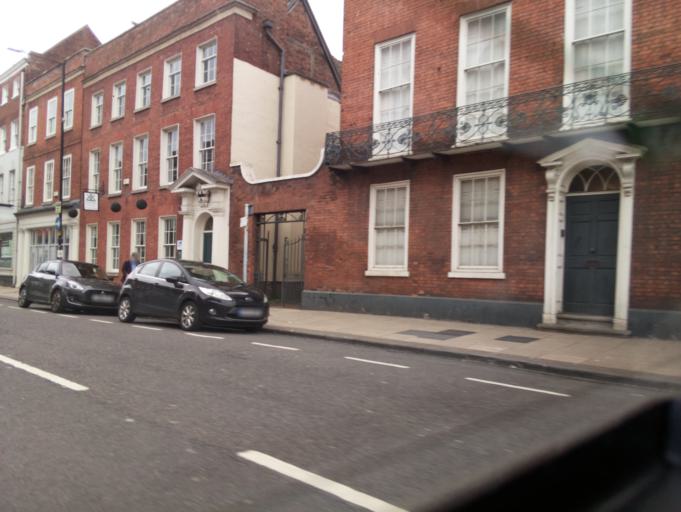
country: GB
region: England
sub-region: Worcestershire
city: Worcester
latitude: 52.1963
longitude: -2.2227
